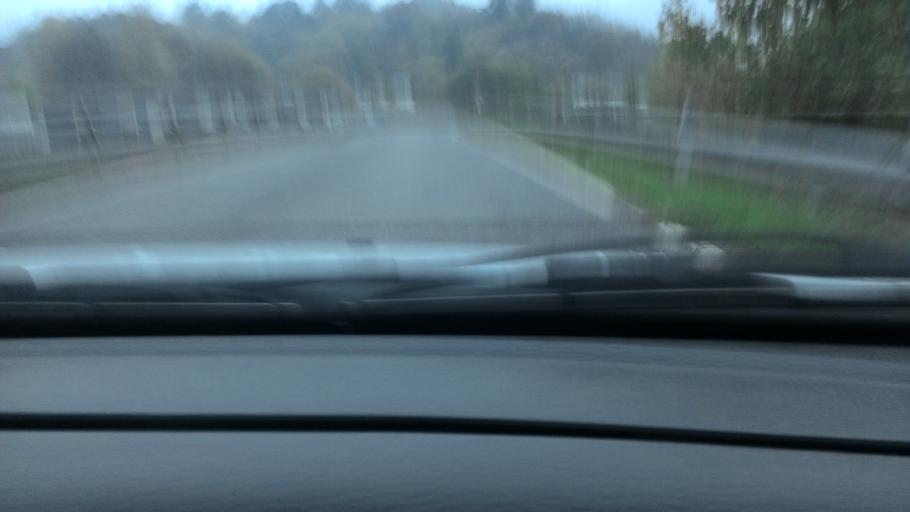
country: IT
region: Piedmont
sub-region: Provincia di Asti
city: Celle Enomondo
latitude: 44.8691
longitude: 8.1155
